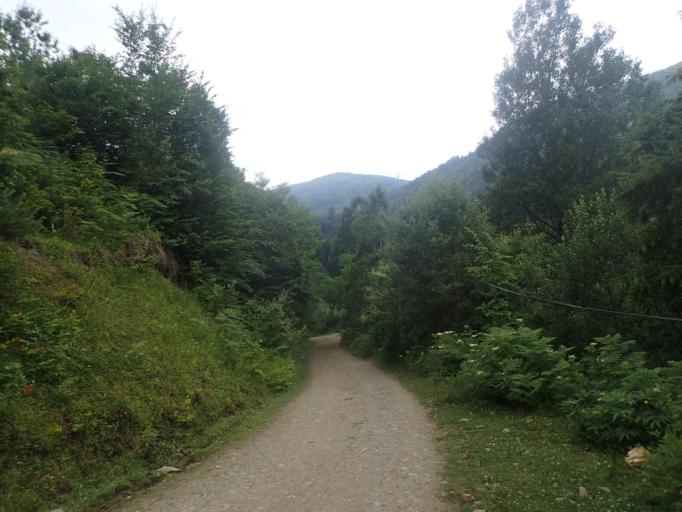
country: TR
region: Ordu
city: Akkus
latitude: 40.8623
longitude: 37.0082
